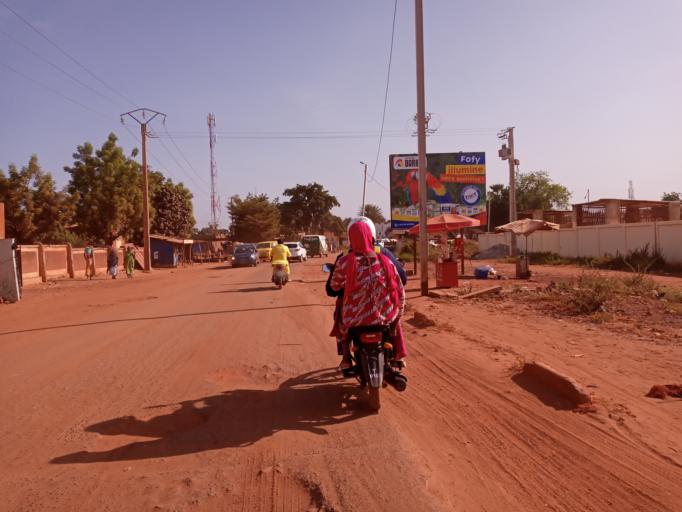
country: ML
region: Bamako
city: Bamako
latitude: 12.6230
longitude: -7.9545
